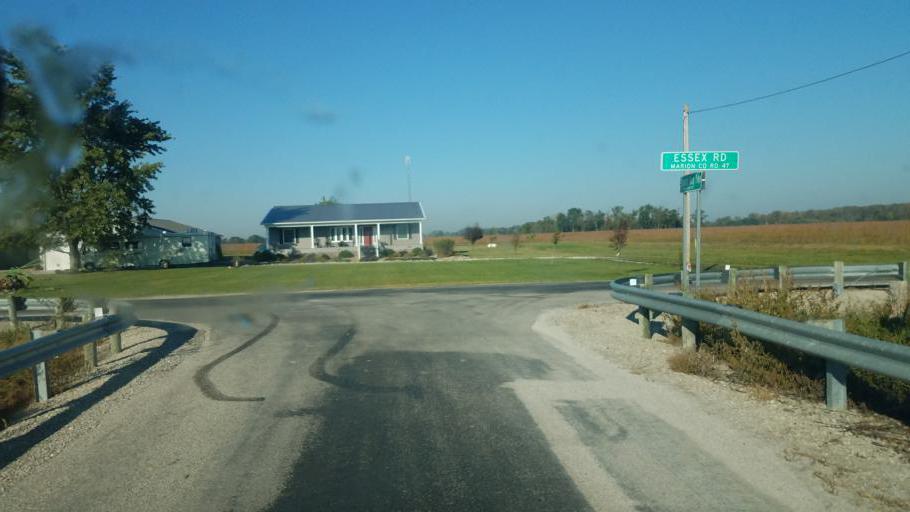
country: US
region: Ohio
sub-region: Union County
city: Richwood
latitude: 40.5481
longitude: -83.3169
